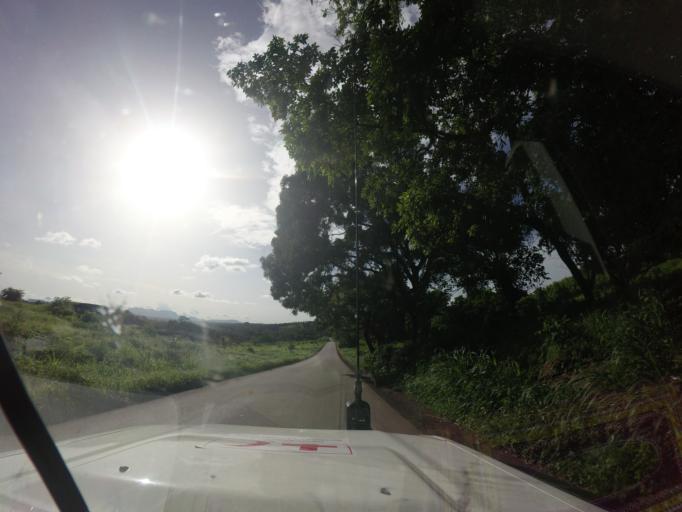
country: GN
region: Kindia
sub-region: Kindia
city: Kindia
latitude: 10.0885
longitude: -12.6150
